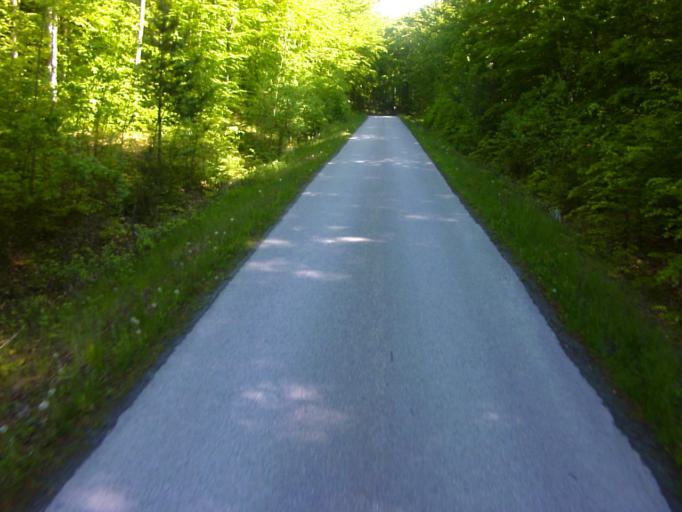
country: SE
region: Blekinge
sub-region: Solvesborgs Kommun
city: Soelvesborg
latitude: 56.0659
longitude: 14.5915
